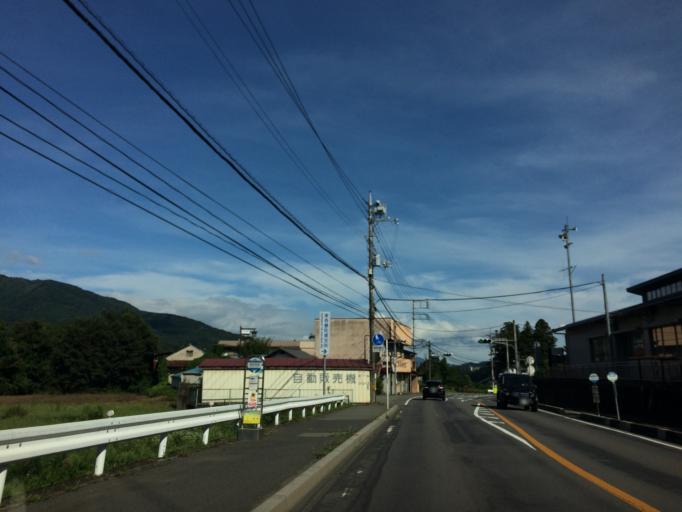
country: JP
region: Gunma
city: Nakanojomachi
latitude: 36.5537
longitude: 138.9011
